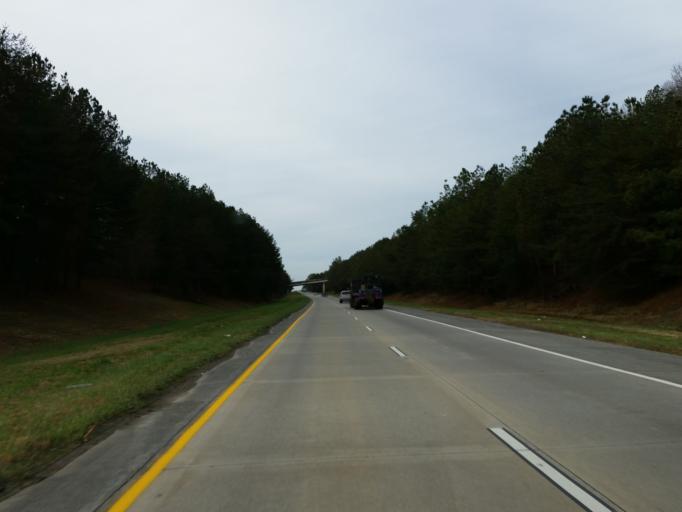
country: US
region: Georgia
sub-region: Cherokee County
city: Canton
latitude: 34.2855
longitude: -84.4466
